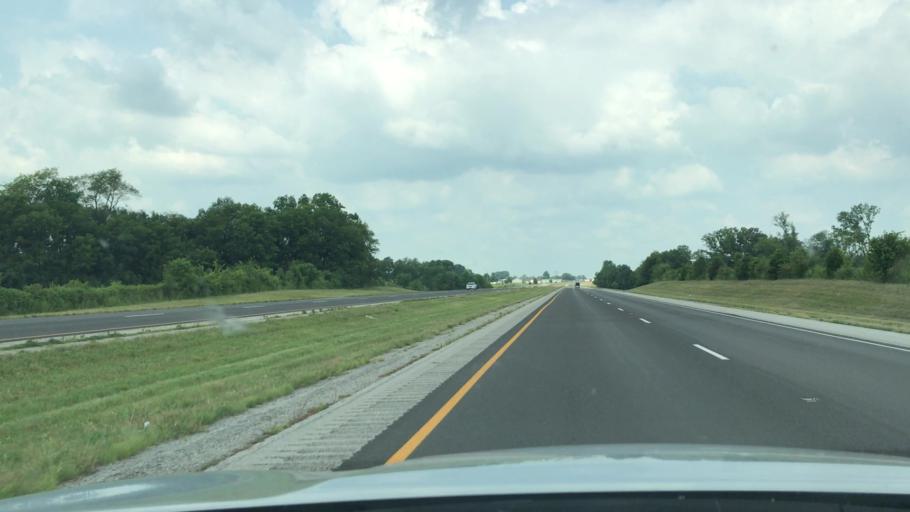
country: US
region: Kentucky
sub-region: Todd County
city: Elkton
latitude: 36.8037
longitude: -87.0789
